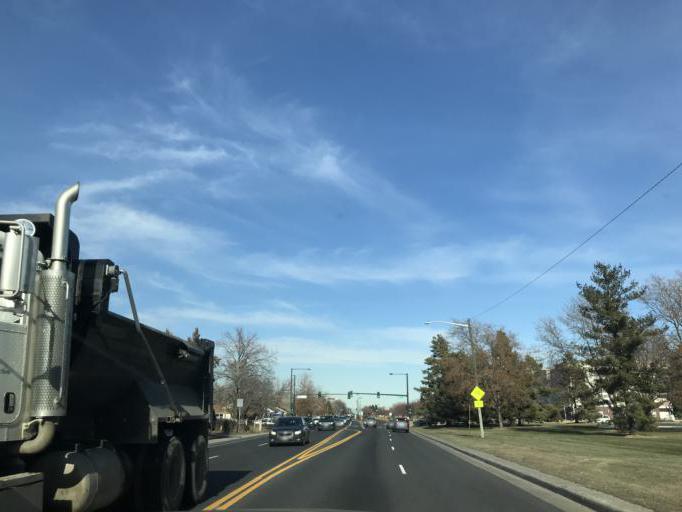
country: US
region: Colorado
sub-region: Arapahoe County
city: Glendale
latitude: 39.7536
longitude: -104.9034
